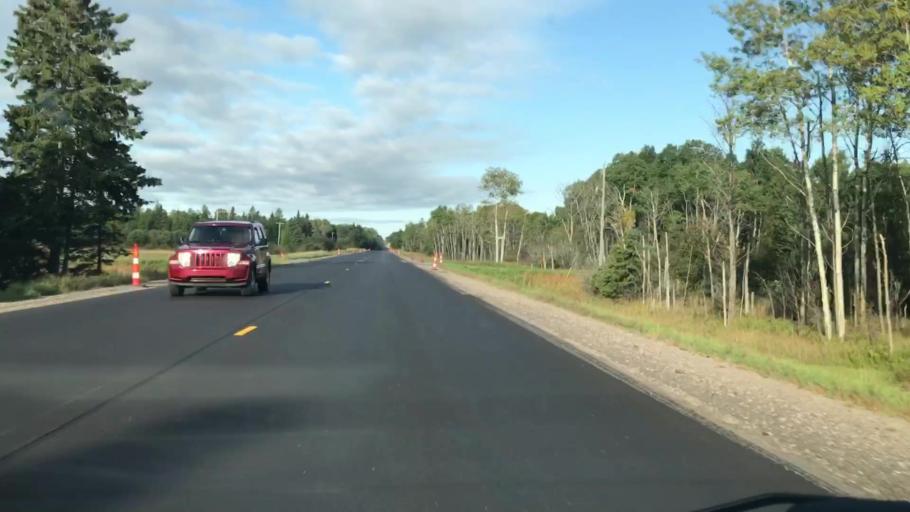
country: US
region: Michigan
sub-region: Mackinac County
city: Saint Ignace
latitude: 46.3460
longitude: -84.9472
